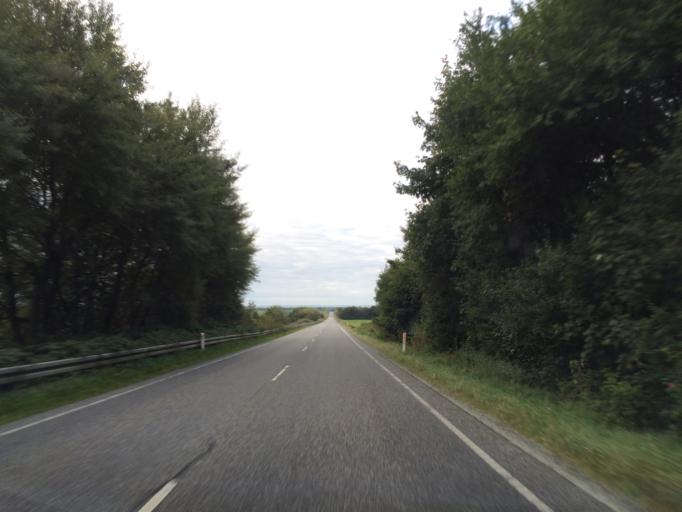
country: DK
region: Central Jutland
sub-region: Ringkobing-Skjern Kommune
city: Skjern
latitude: 56.0139
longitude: 8.5030
